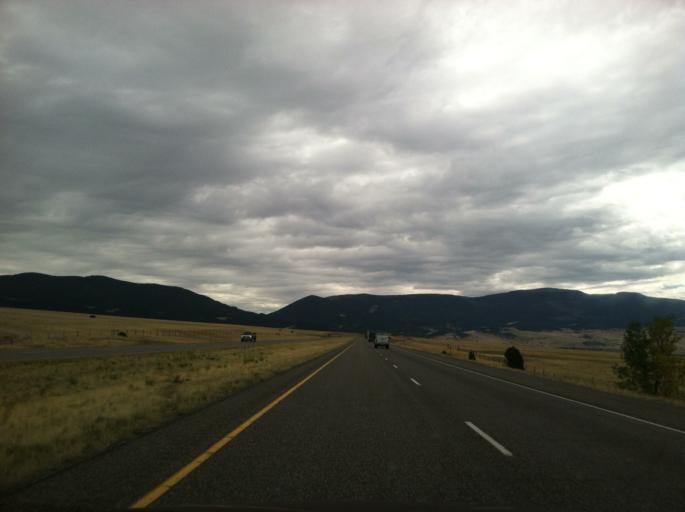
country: US
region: Montana
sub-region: Park County
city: Livingston
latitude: 45.6620
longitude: -110.5302
